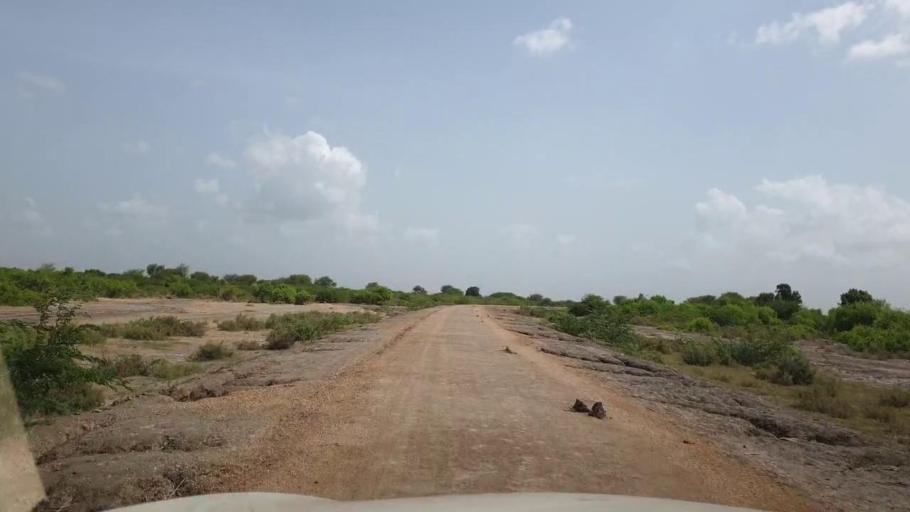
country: PK
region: Sindh
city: Kadhan
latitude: 24.3928
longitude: 68.7947
